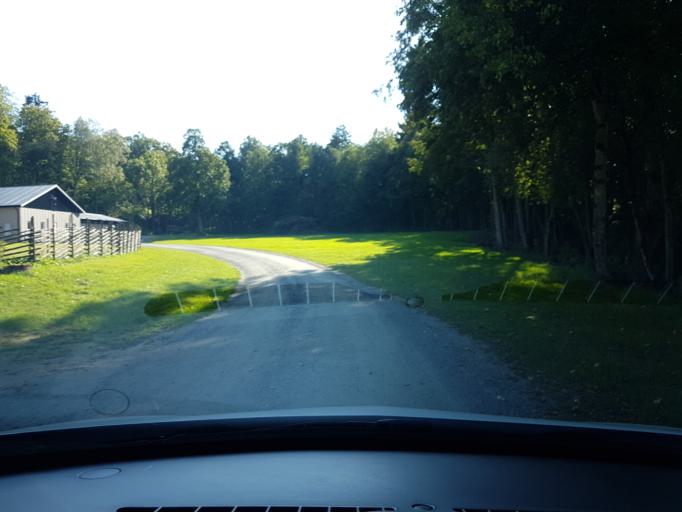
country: SE
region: Vaestra Goetaland
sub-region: Ale Kommun
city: Skepplanda
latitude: 57.9763
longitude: 12.1935
